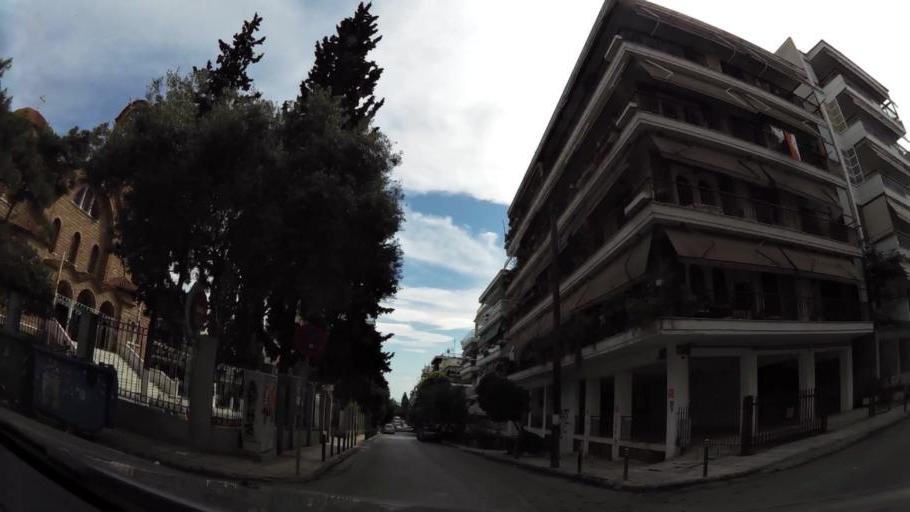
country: GR
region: Central Macedonia
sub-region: Nomos Thessalonikis
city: Kalamaria
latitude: 40.5765
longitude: 22.9510
